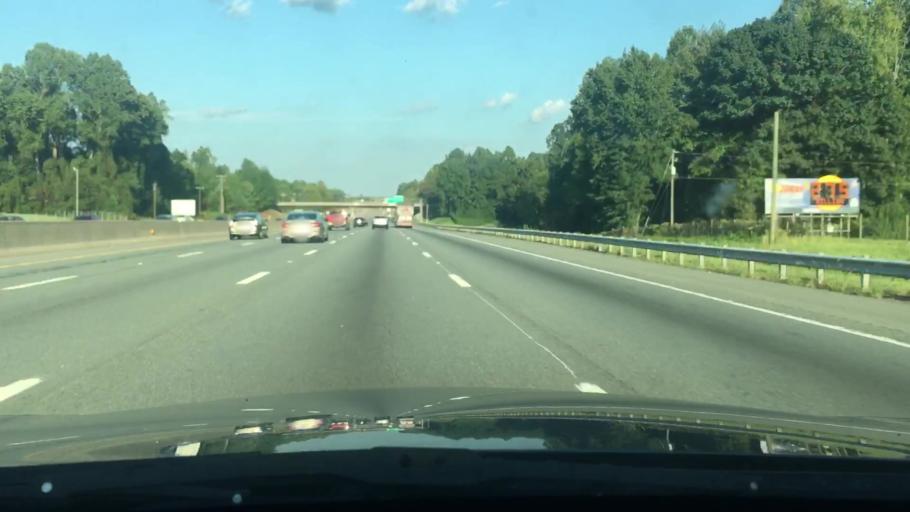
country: US
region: North Carolina
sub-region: Alamance County
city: Mebane
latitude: 36.0783
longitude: -79.2482
